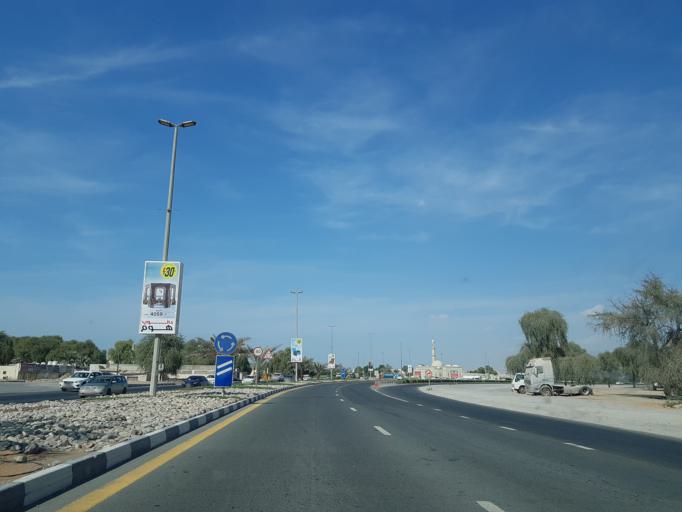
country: AE
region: Ra's al Khaymah
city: Ras al-Khaimah
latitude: 25.7110
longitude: 55.9701
